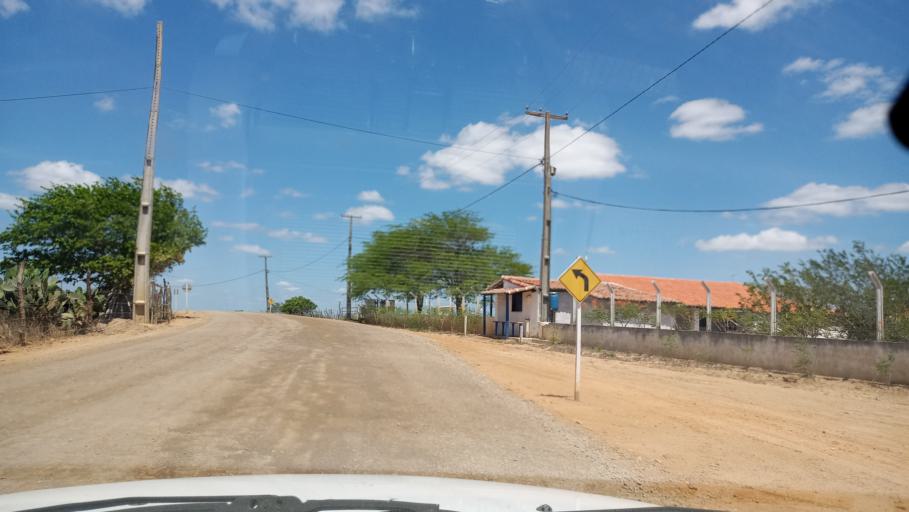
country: BR
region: Rio Grande do Norte
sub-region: Sao Paulo Do Potengi
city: Sao Paulo do Potengi
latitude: -5.7817
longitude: -35.9143
